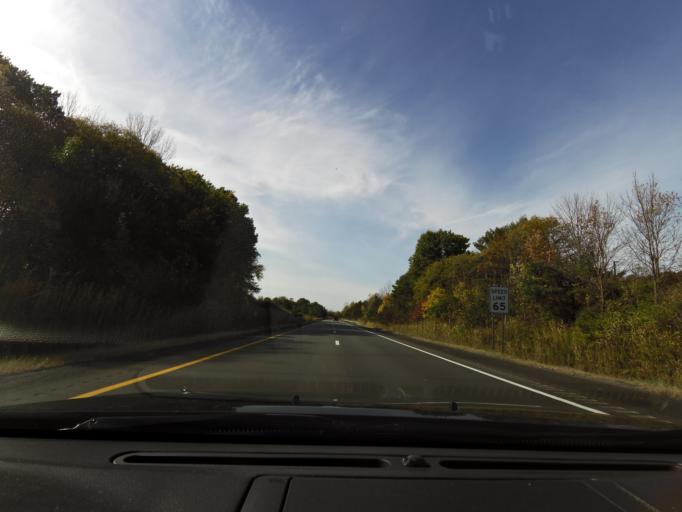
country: US
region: New York
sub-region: Erie County
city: Billington Heights
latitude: 42.7973
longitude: -78.6251
